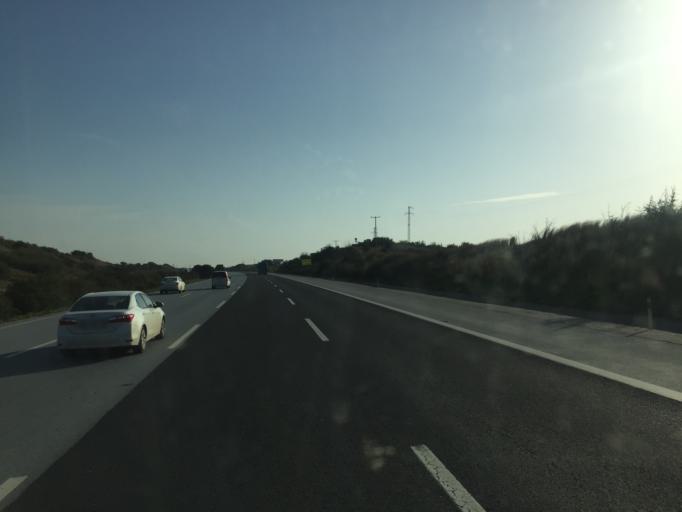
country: TR
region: Mersin
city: Yenice
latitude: 37.0225
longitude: 35.0894
